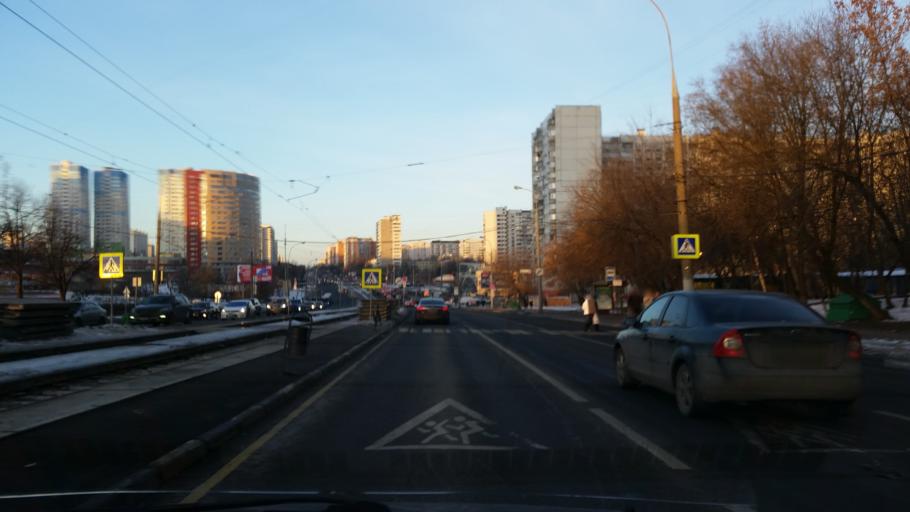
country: RU
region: Moscow
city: Nagornyy
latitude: 55.6375
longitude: 37.6051
